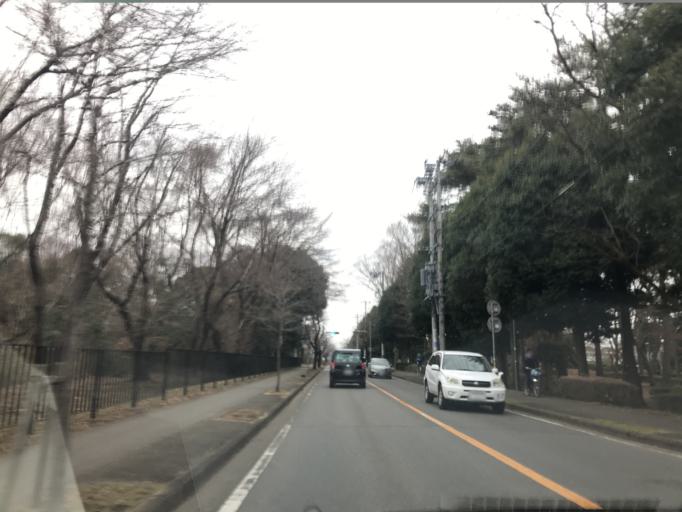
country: JP
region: Ibaraki
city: Naka
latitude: 36.0531
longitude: 140.1286
